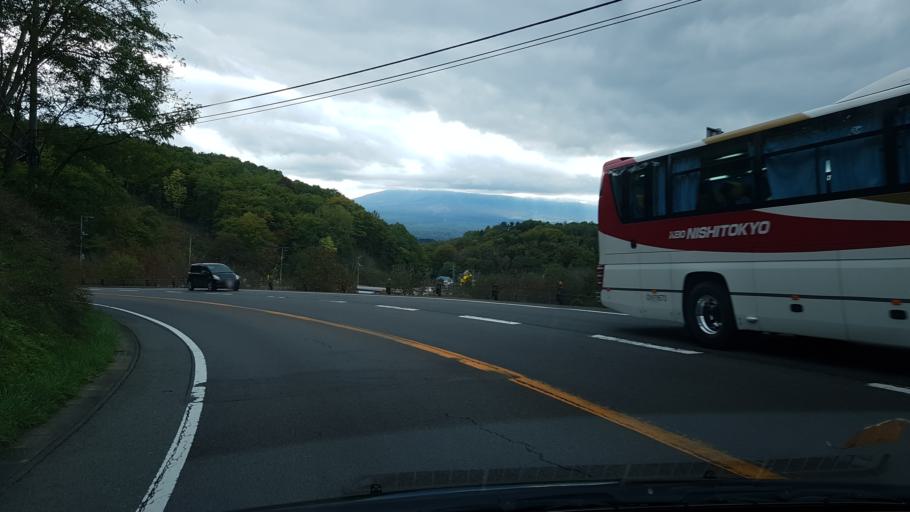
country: JP
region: Gunma
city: Nakanojomachi
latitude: 36.5991
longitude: 138.5867
